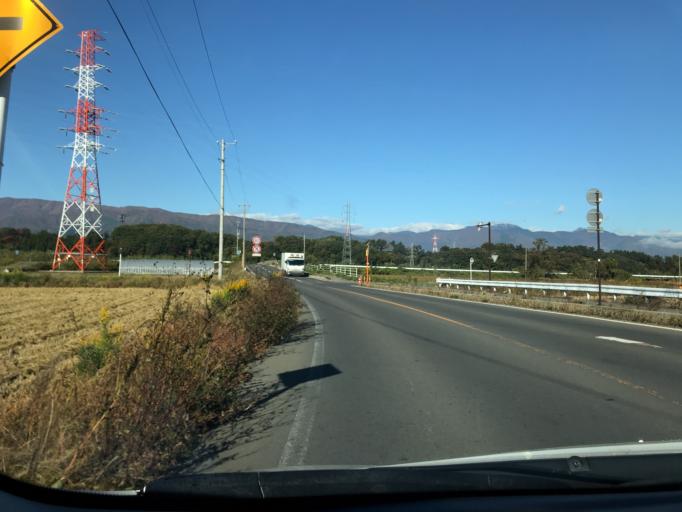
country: JP
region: Nagano
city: Shiojiri
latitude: 36.1314
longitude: 137.9315
